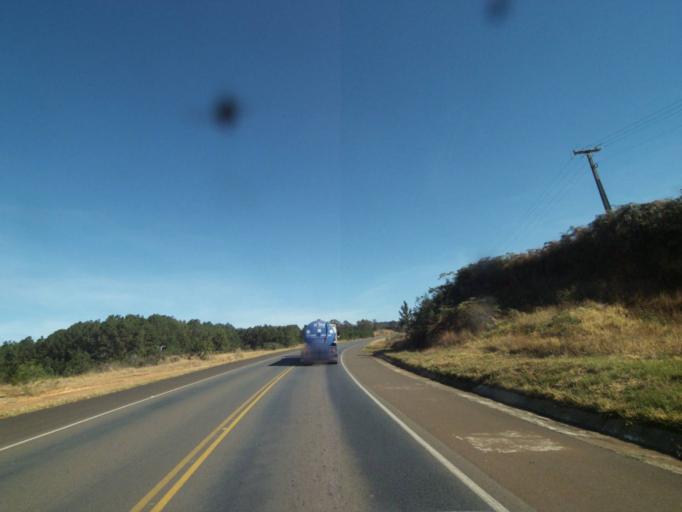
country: BR
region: Parana
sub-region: Tibagi
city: Tibagi
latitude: -24.4896
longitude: -50.4388
